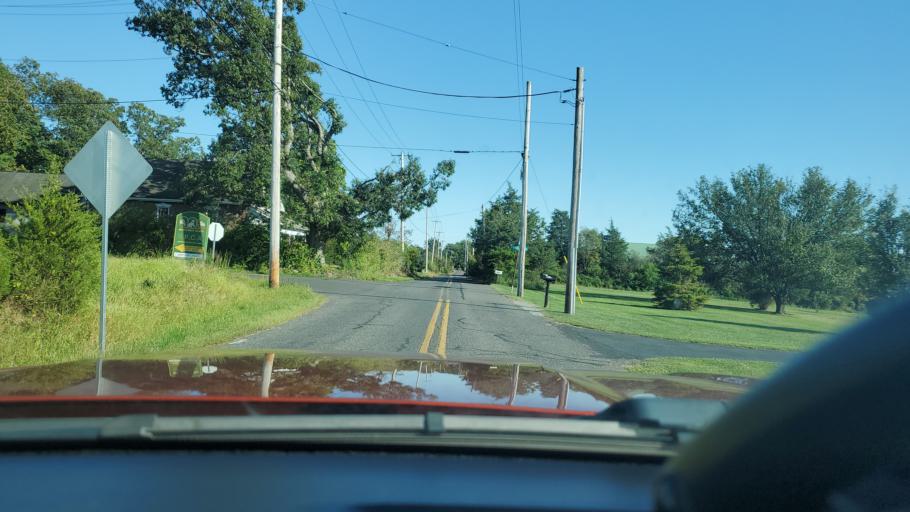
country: US
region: Pennsylvania
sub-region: Montgomery County
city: Woxall
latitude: 40.3099
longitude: -75.5154
